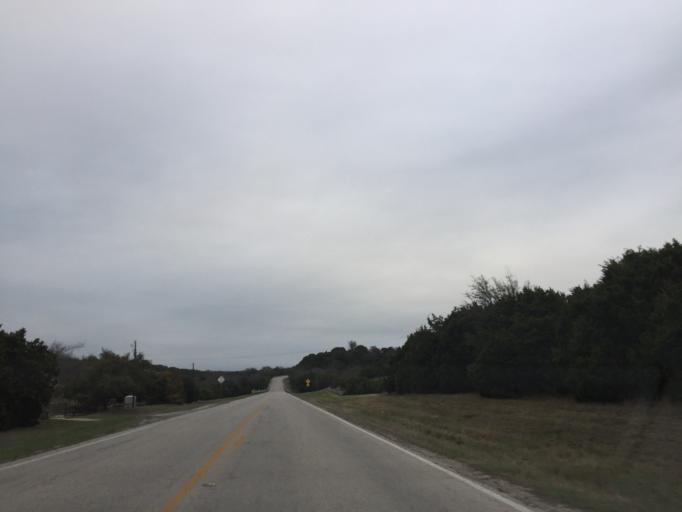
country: US
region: Texas
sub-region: Coryell County
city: Ames
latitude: 31.4998
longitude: -97.7278
